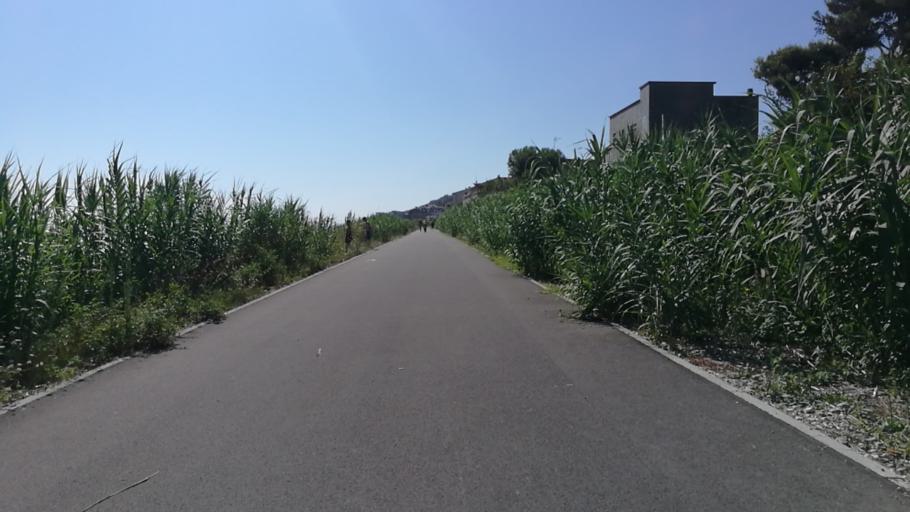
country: IT
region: Abruzzo
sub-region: Provincia di Chieti
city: Marina di San Vito
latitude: 42.3208
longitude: 14.4315
